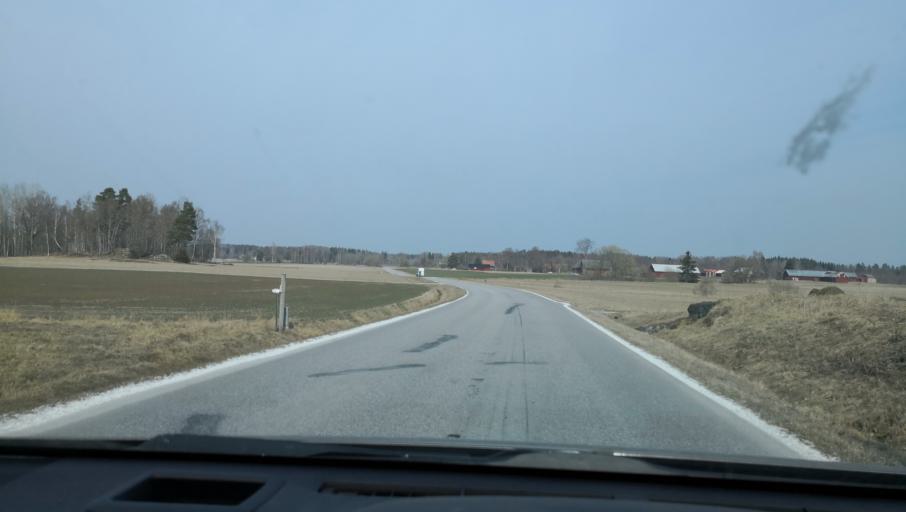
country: SE
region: OErebro
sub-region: Lindesbergs Kommun
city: Frovi
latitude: 59.3332
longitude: 15.4426
